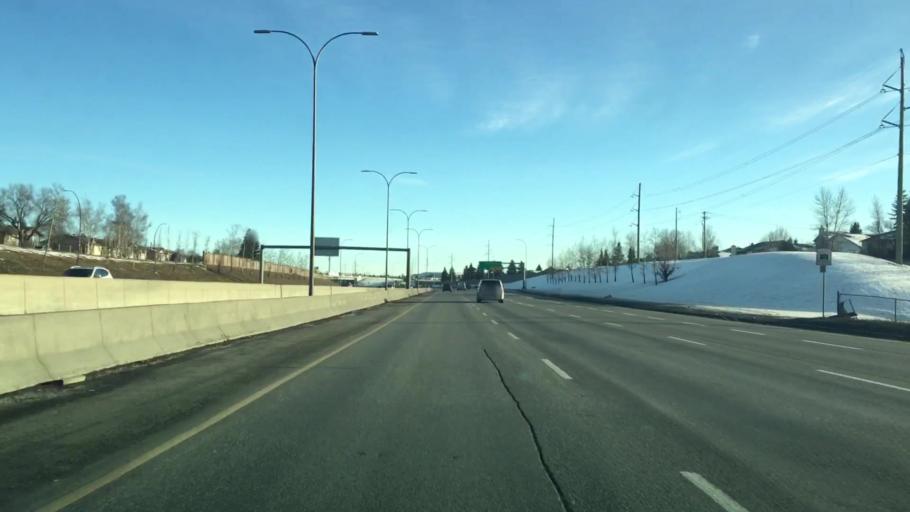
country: CA
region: Alberta
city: Calgary
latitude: 50.9853
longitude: -114.0232
